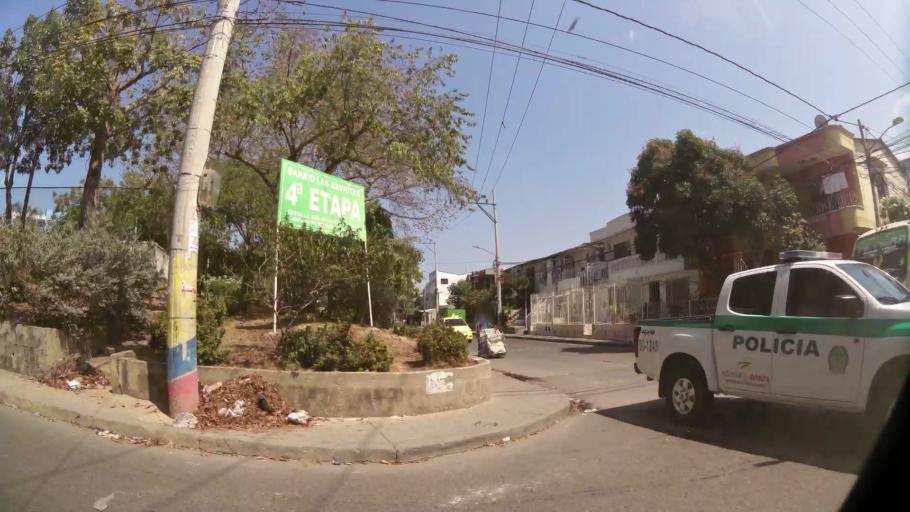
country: CO
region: Bolivar
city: Cartagena
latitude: 10.4014
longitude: -75.4883
